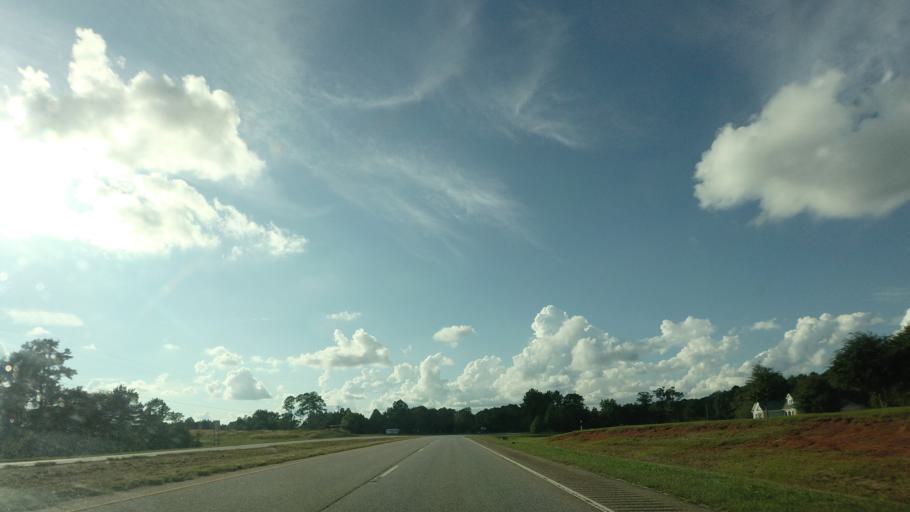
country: US
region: Georgia
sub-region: Pulaski County
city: Hawkinsville
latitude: 32.3261
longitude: -83.5588
